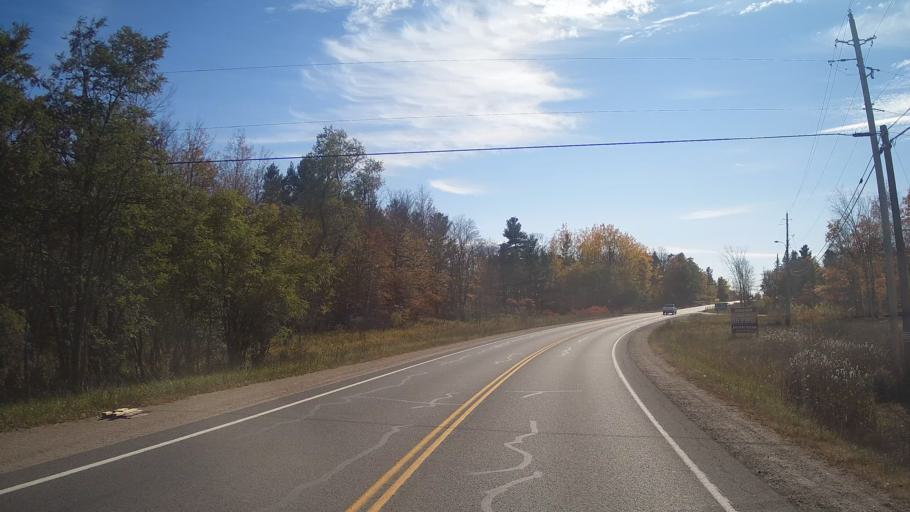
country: CA
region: Ontario
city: Perth
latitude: 44.7924
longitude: -76.6774
